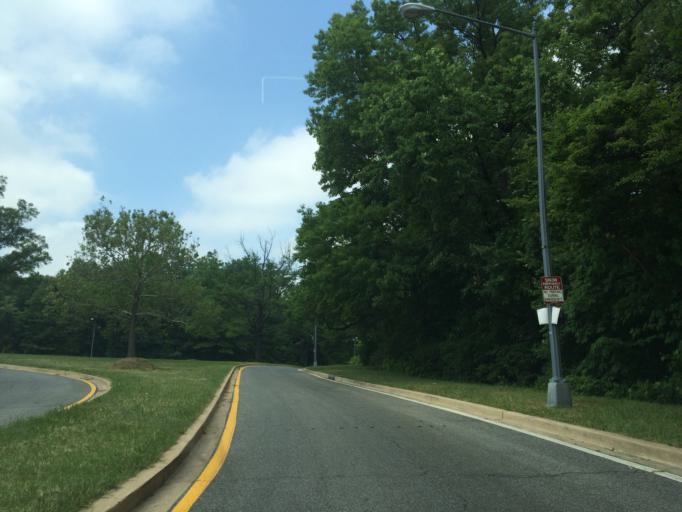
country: US
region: Maryland
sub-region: Prince George's County
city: Chillum
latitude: 38.9322
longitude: -77.0053
